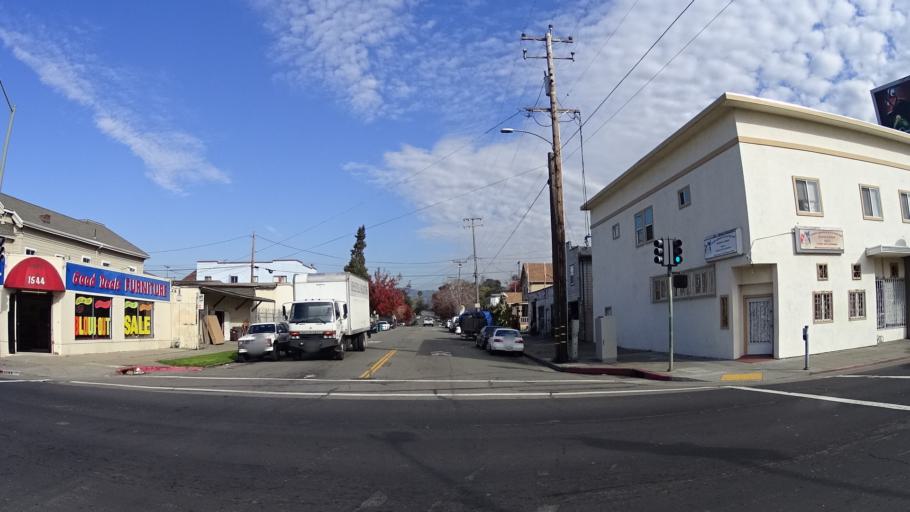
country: US
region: California
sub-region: Alameda County
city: Alameda
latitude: 37.7883
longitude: -122.2442
